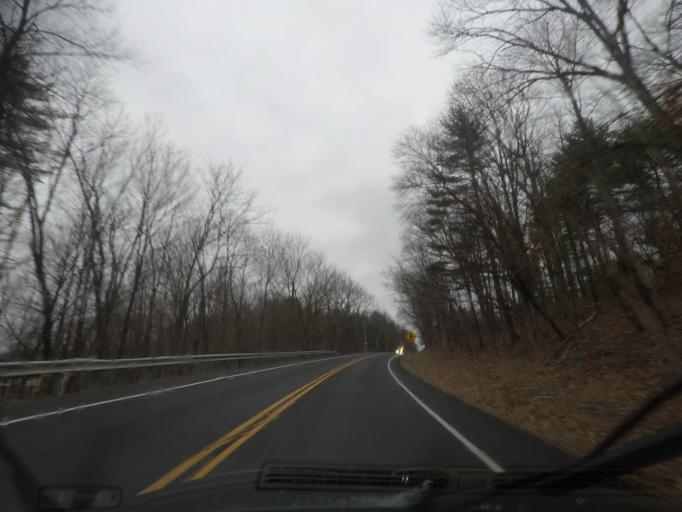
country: US
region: New York
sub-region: Rensselaer County
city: East Greenbush
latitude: 42.5981
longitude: -73.6460
